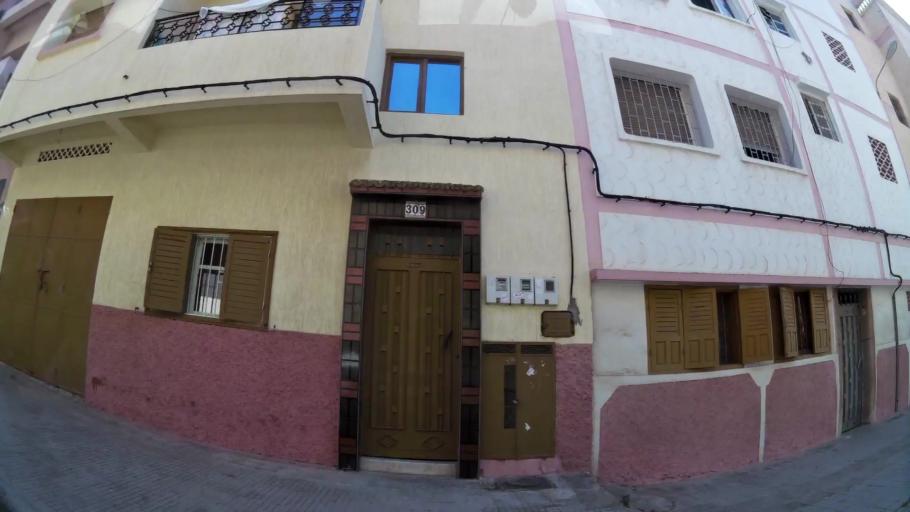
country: MA
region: Rabat-Sale-Zemmour-Zaer
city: Sale
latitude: 34.0449
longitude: -6.7907
